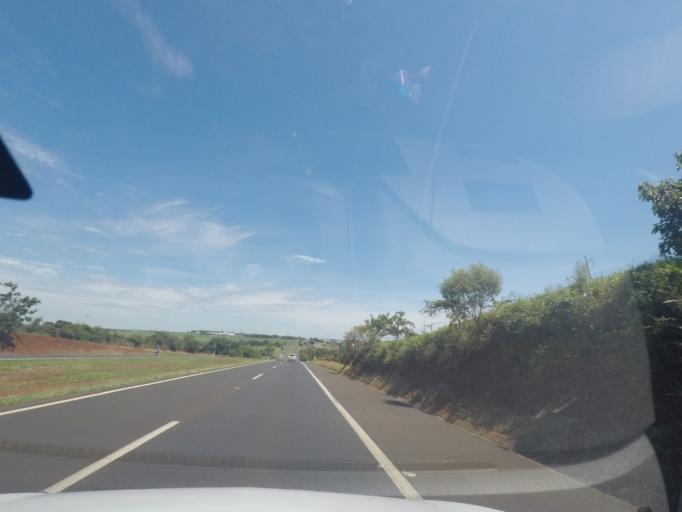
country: BR
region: Sao Paulo
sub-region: Araraquara
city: Araraquara
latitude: -21.8023
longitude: -48.2006
